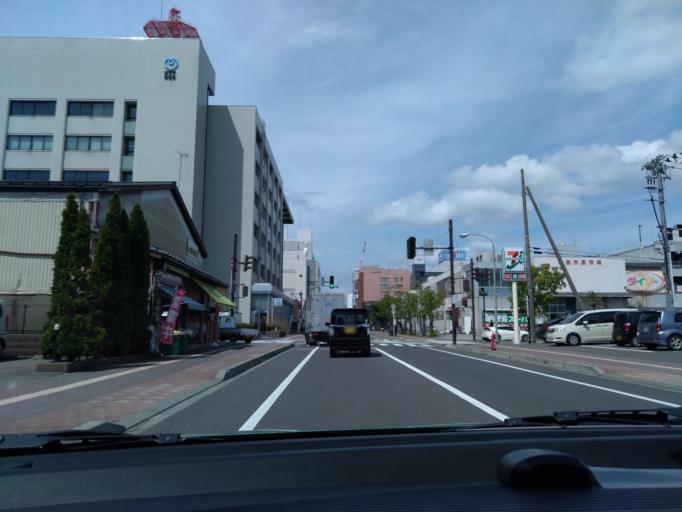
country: JP
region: Akita
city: Akita
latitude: 39.7139
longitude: 140.1250
